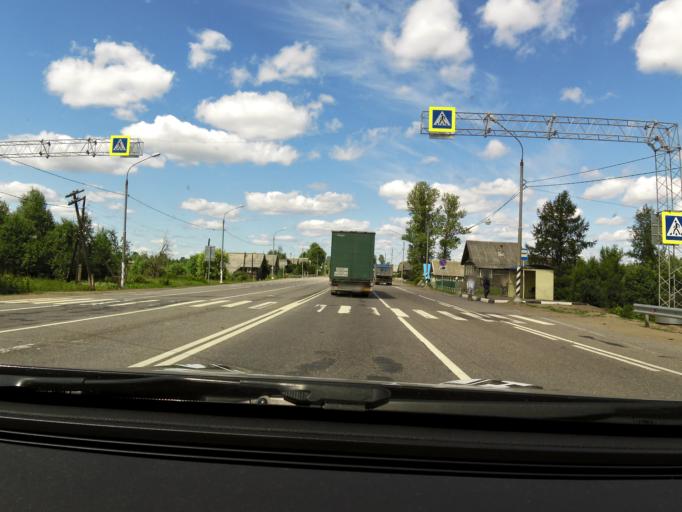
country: RU
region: Tverskaya
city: Kuzhenkino
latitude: 57.7626
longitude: 33.9494
